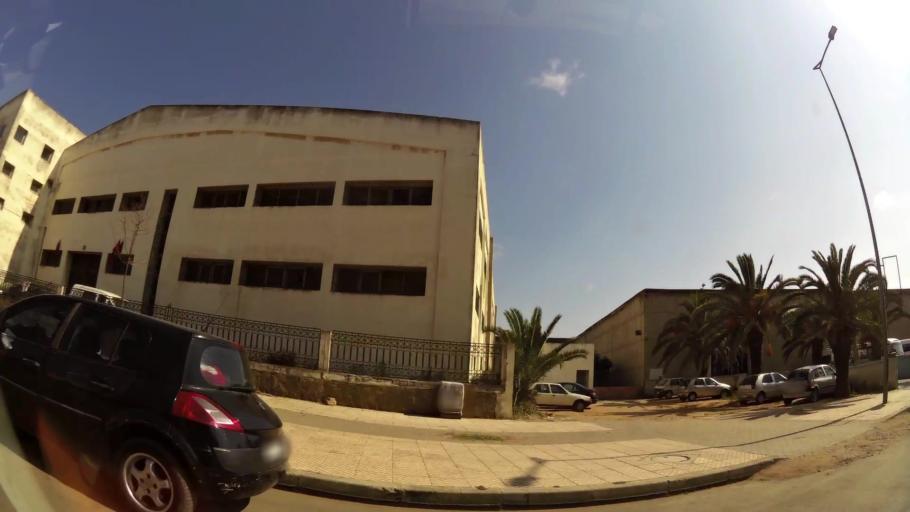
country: MA
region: Rabat-Sale-Zemmour-Zaer
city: Sale
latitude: 34.0397
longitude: -6.7829
